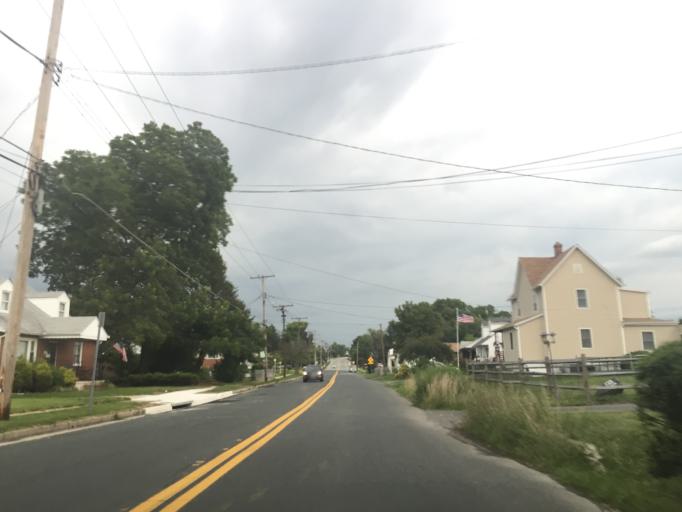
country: US
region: Maryland
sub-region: Baltimore County
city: Parkville
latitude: 39.3832
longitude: -76.5437
